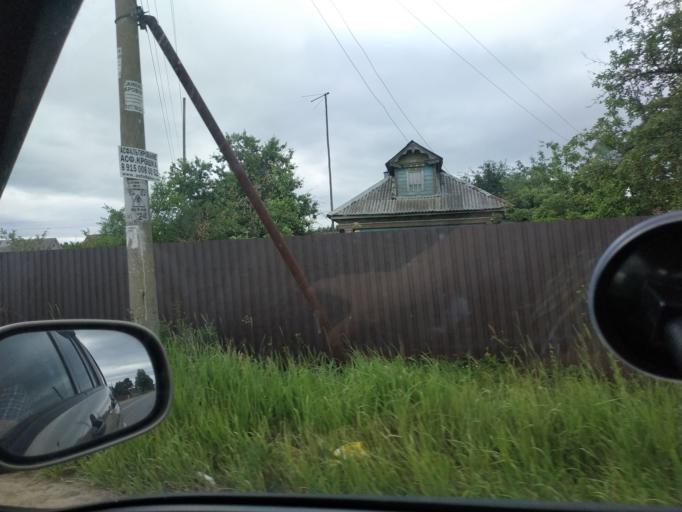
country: RU
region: Moskovskaya
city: Chernogolovka
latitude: 56.0668
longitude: 38.2596
